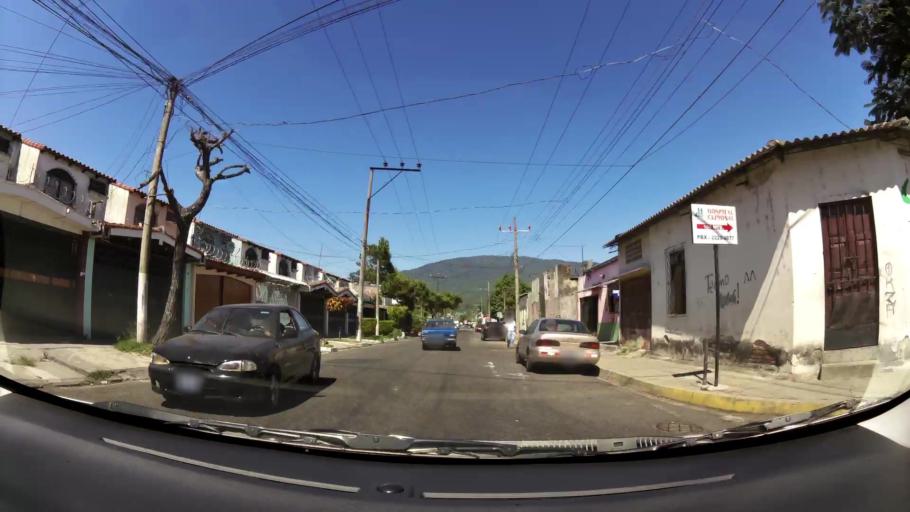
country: SV
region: La Libertad
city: Santa Tecla
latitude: 13.6714
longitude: -89.2950
